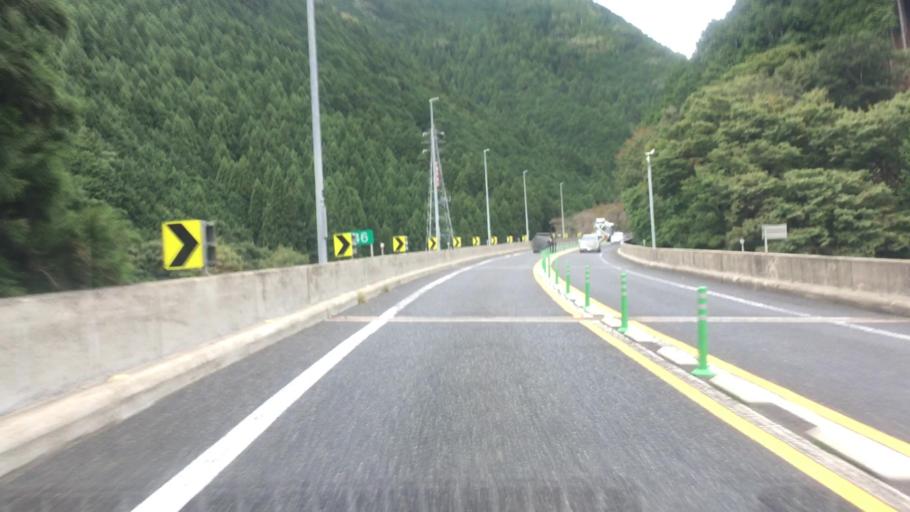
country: JP
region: Kyoto
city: Fukuchiyama
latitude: 35.2923
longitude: 134.9587
